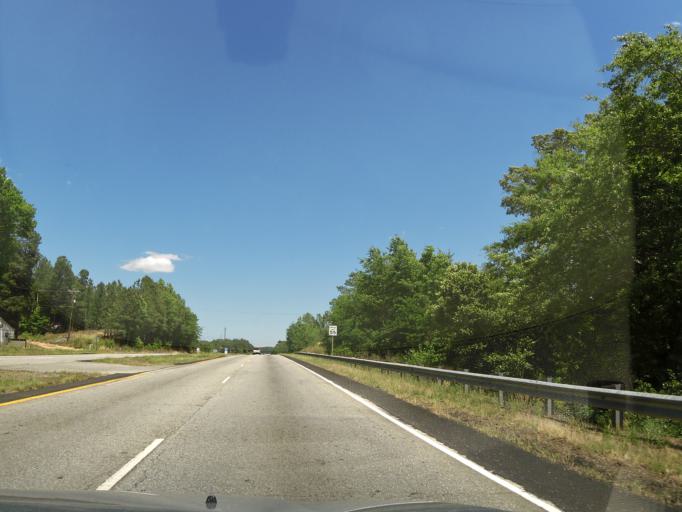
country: US
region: South Carolina
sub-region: Aiken County
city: Warrenville
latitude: 33.5570
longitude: -81.7992
